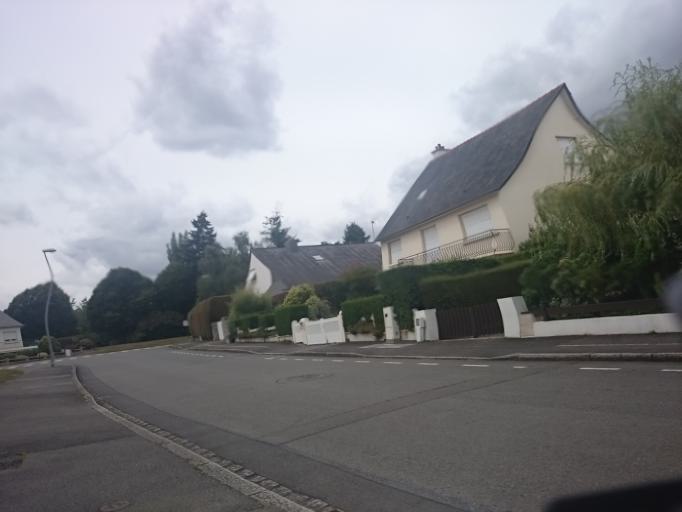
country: FR
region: Brittany
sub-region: Departement d'Ille-et-Vilaine
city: Cesson-Sevigne
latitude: 48.1212
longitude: -1.6142
